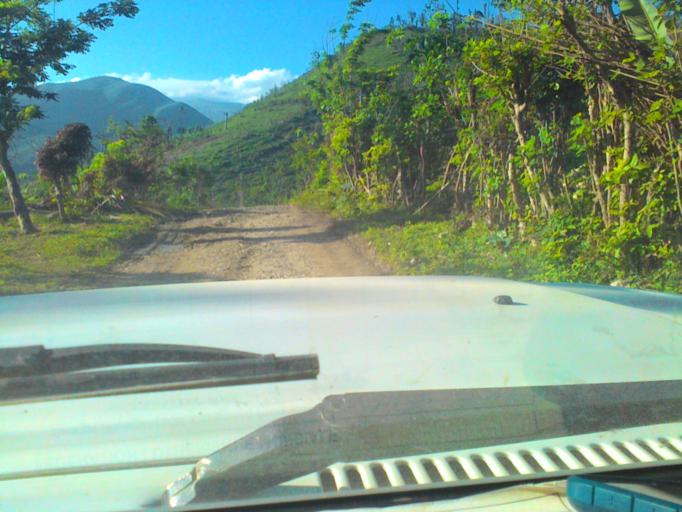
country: HT
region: Grandans
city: Jeremie
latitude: 18.5140
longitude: -74.0829
